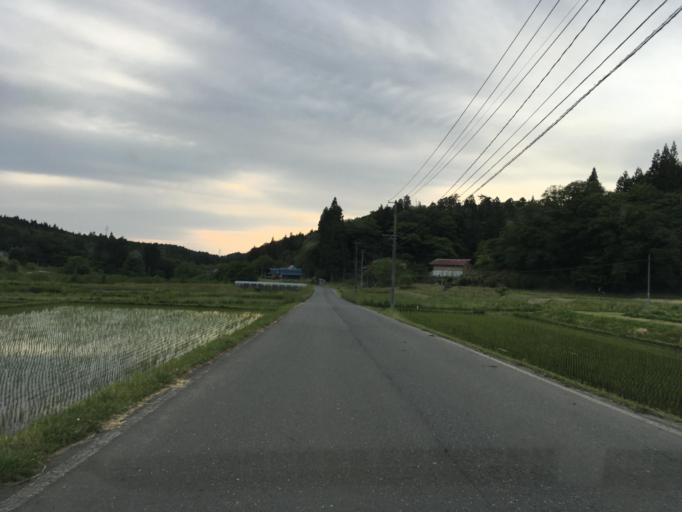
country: JP
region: Iwate
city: Mizusawa
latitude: 39.1639
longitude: 141.3102
